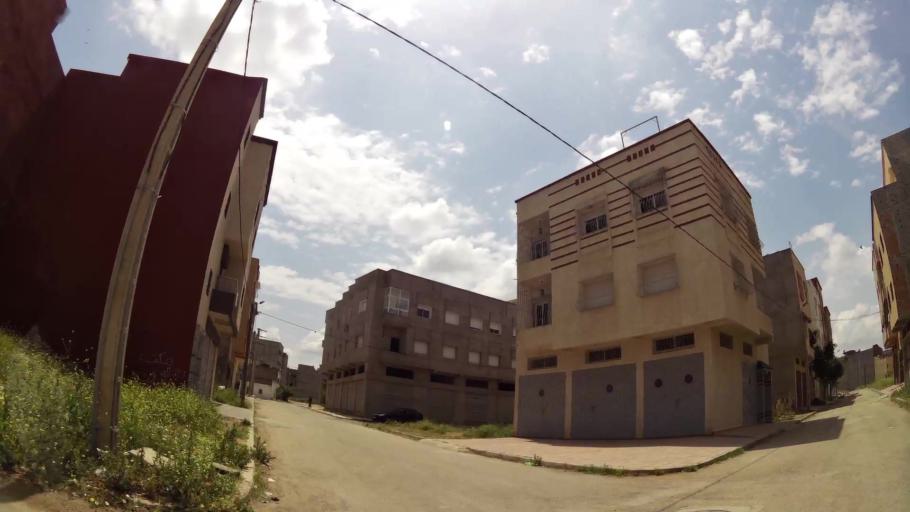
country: MA
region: Gharb-Chrarda-Beni Hssen
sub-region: Kenitra Province
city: Kenitra
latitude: 34.0092
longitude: -6.5367
